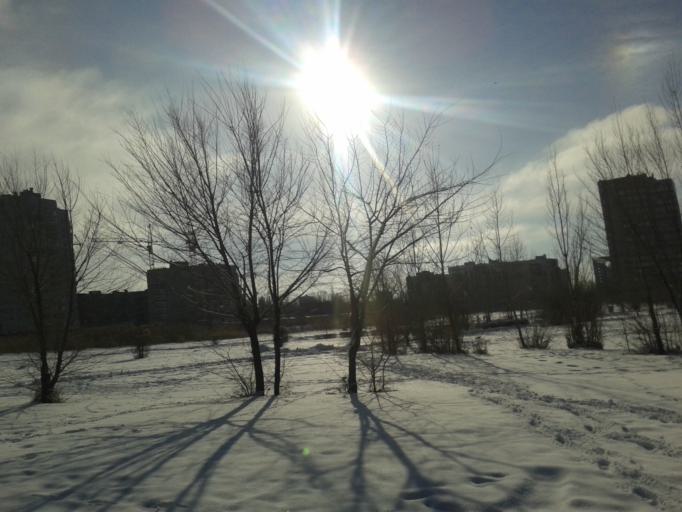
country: RU
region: Volgograd
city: Volgograd
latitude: 48.7479
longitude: 44.4999
